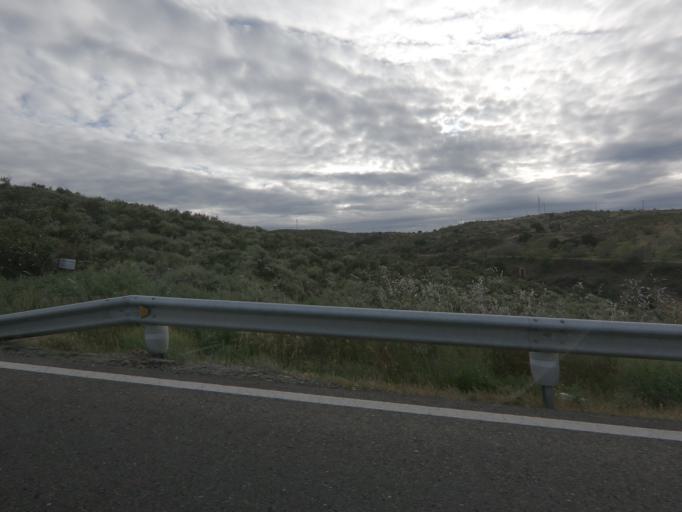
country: ES
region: Extremadura
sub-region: Provincia de Caceres
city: Coria
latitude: 39.9520
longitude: -6.5094
